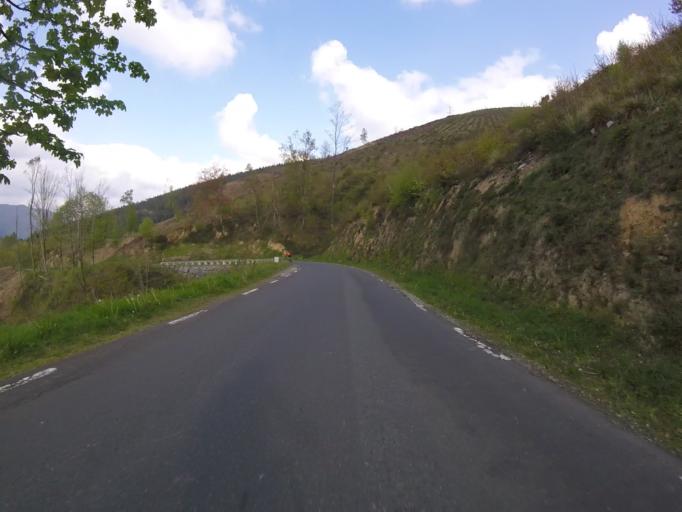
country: ES
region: Basque Country
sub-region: Provincia de Guipuzcoa
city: Azkoitia
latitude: 43.2056
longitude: -2.3552
